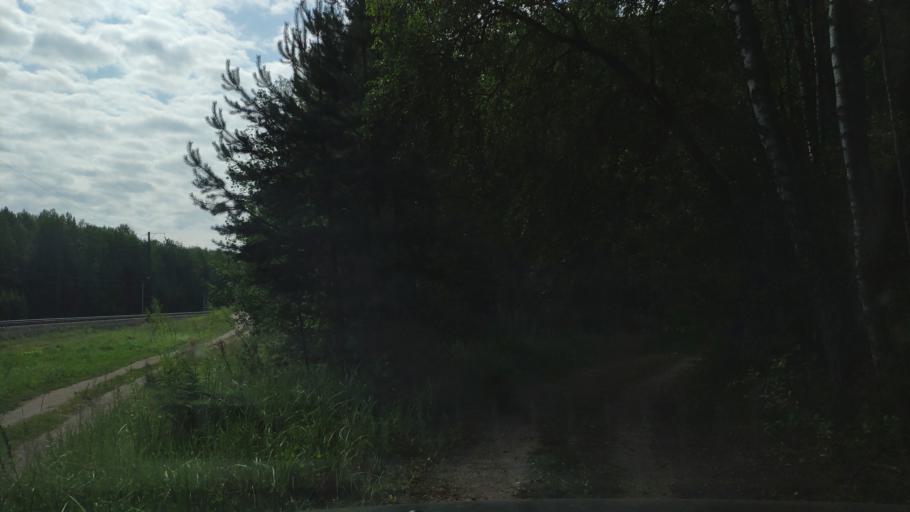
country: BY
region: Minsk
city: Khatsyezhyna
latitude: 53.9606
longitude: 27.3066
